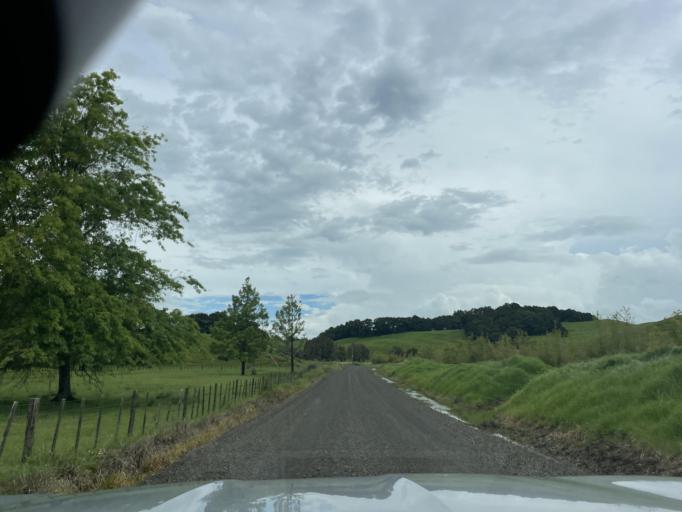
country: NZ
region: Northland
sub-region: Whangarei
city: Maungatapere
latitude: -35.8138
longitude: 174.0367
